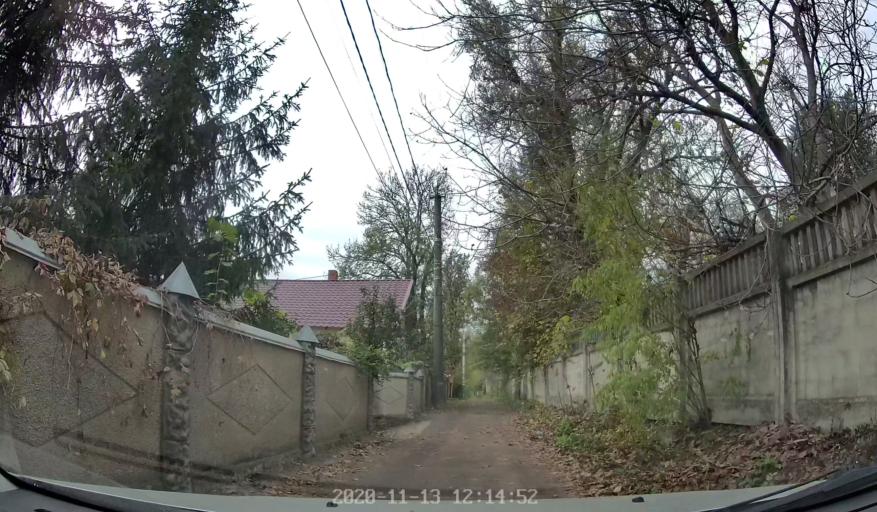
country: MD
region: Laloveni
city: Ialoveni
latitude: 46.9521
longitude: 28.8378
